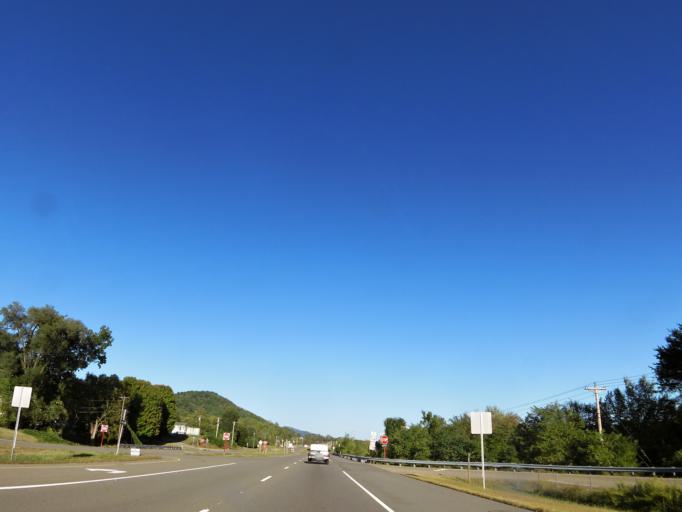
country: US
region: Tennessee
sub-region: Grainger County
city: Bean Station
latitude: 36.3446
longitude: -83.3242
